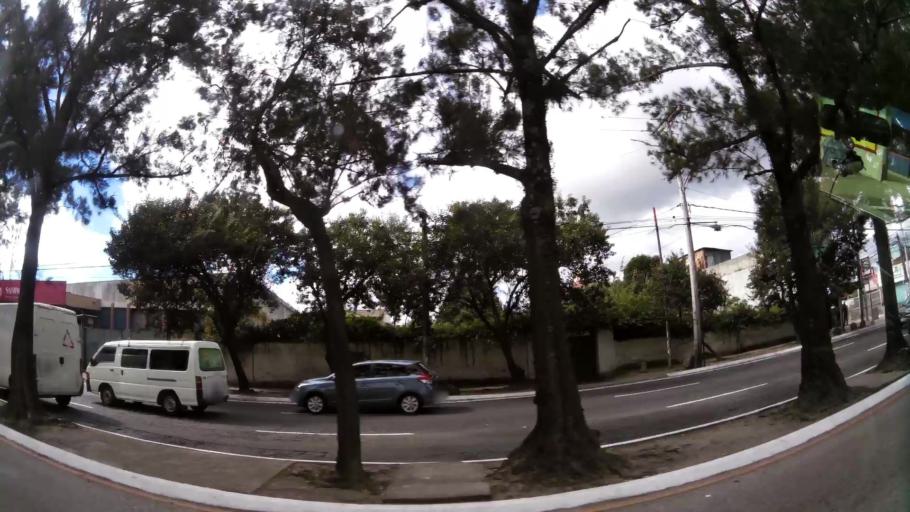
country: GT
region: Guatemala
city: Guatemala City
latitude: 14.6214
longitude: -90.5460
